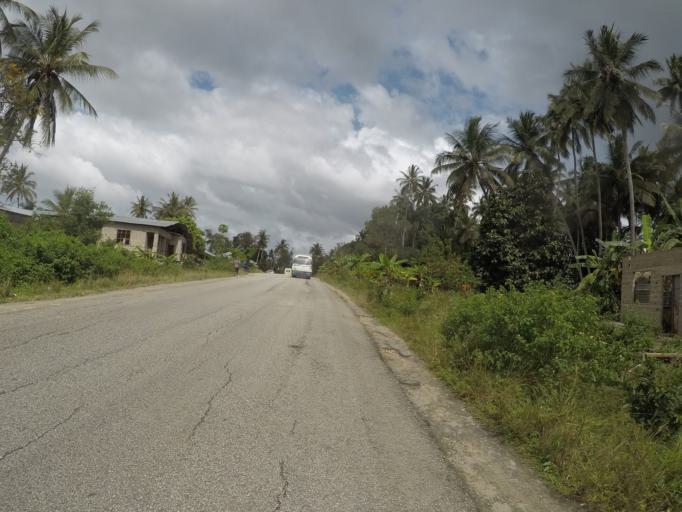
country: TZ
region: Zanzibar North
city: Mkokotoni
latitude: -5.9094
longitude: 39.2522
